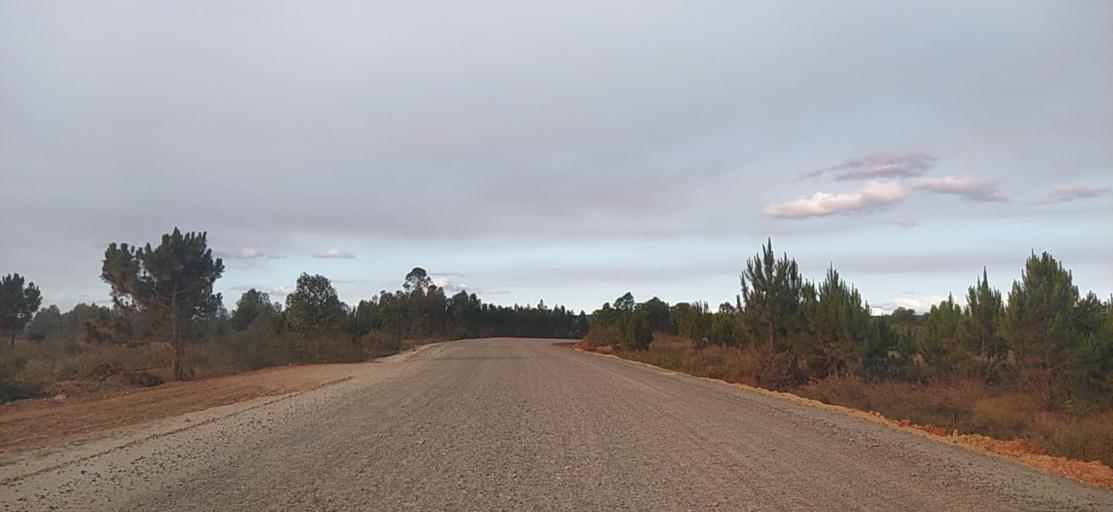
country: MG
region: Analamanga
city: Anjozorobe
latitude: -18.5065
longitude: 48.2636
